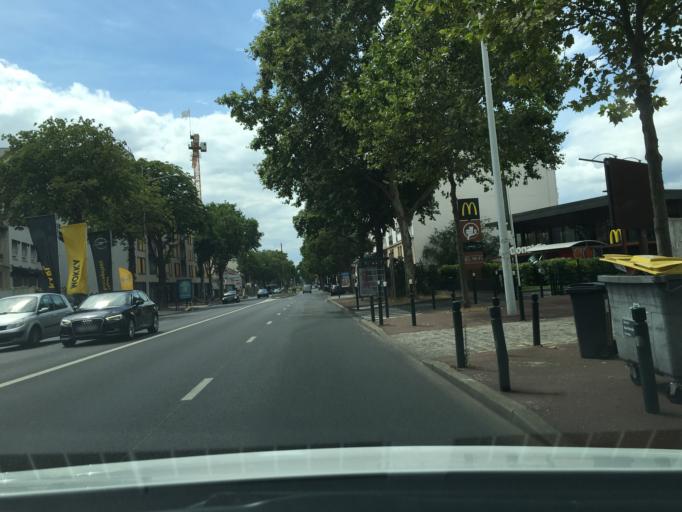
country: FR
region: Ile-de-France
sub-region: Departement des Hauts-de-Seine
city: Rueil-Malmaison
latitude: 48.8852
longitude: 2.1953
